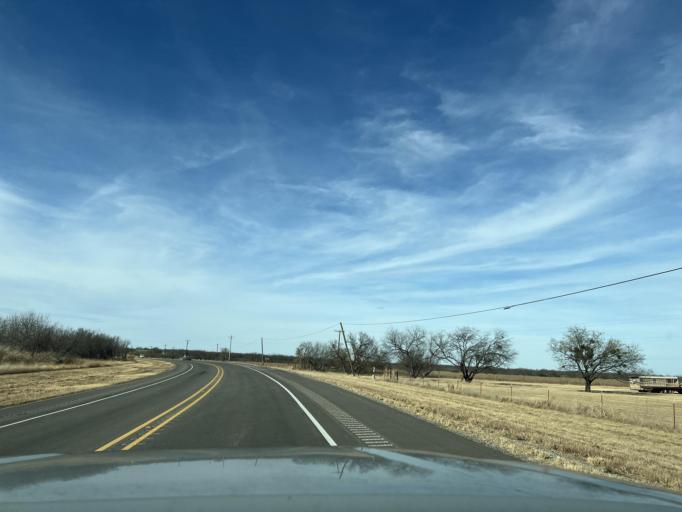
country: US
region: Texas
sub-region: Shackelford County
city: Albany
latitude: 32.5875
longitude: -99.1846
